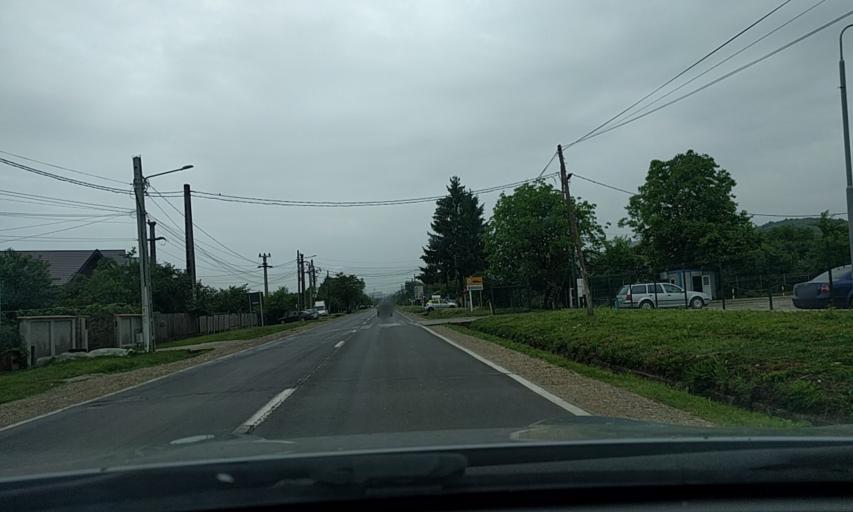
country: RO
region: Dambovita
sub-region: Comuna Aninoasa
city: Aninoasa
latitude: 44.9679
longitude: 25.4346
